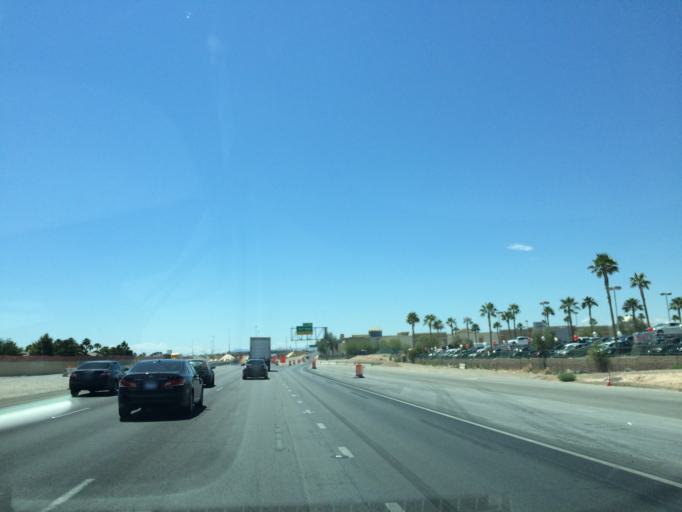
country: US
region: Nevada
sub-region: Clark County
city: Las Vegas
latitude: 36.2690
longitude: -115.2593
